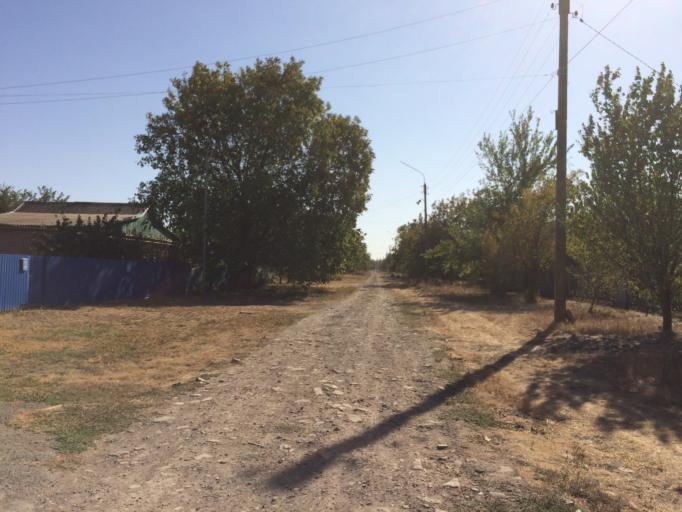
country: RU
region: Rostov
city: Tselina
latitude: 46.5252
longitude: 41.1837
